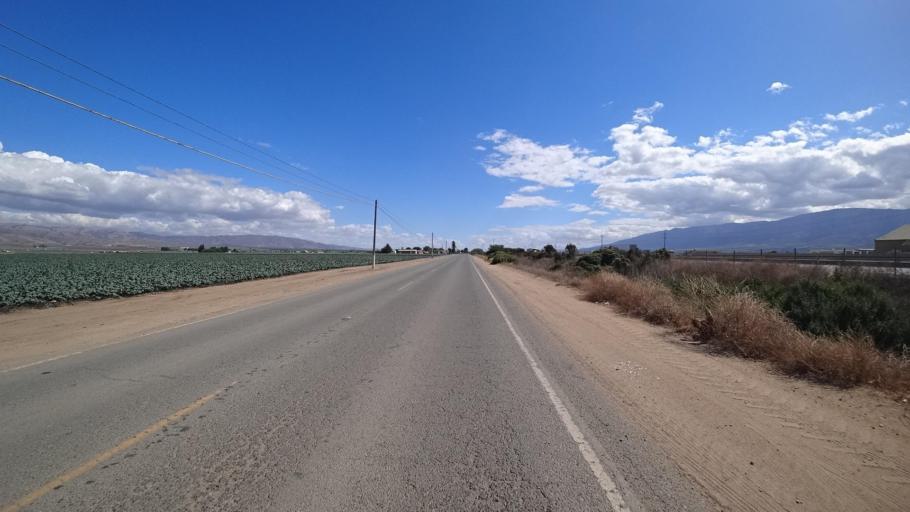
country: US
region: California
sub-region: Monterey County
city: Gonzales
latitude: 36.5286
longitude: -121.4696
